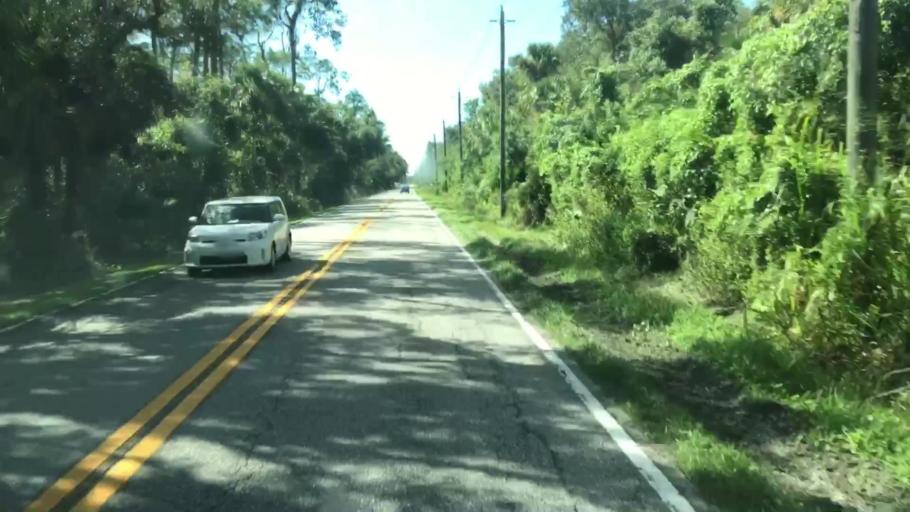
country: US
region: Florida
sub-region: Lee County
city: Alva
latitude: 26.7260
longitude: -81.6502
